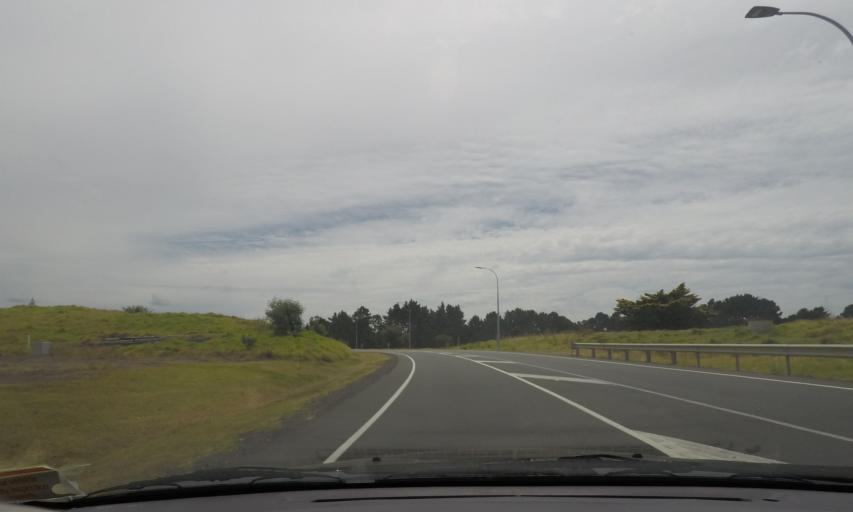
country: NZ
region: Auckland
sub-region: Auckland
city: Mangere
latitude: -36.9961
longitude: 174.7998
